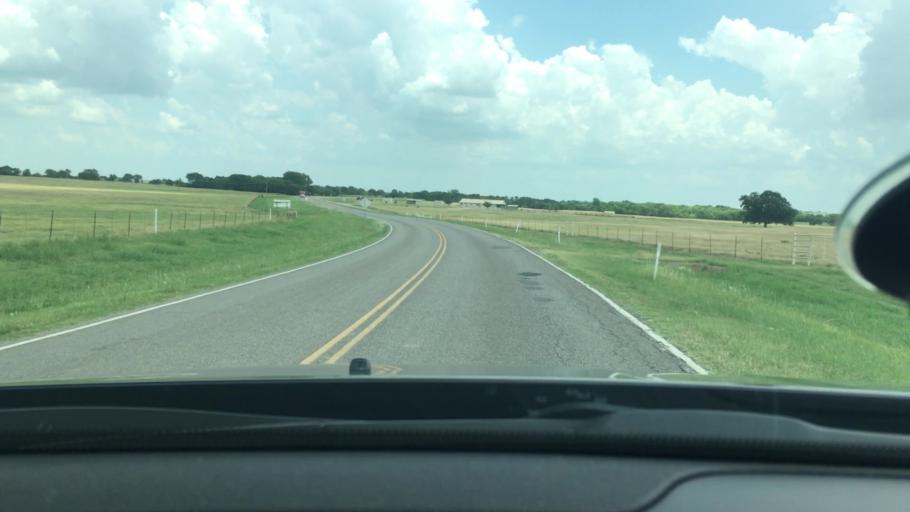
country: US
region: Oklahoma
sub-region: Love County
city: Marietta
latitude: 33.9369
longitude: -97.1063
